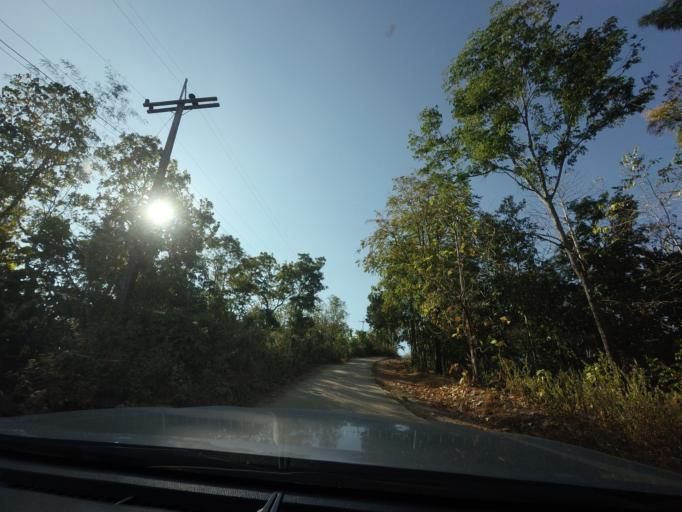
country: TH
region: Lampang
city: Chae Hom
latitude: 18.6144
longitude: 99.6578
